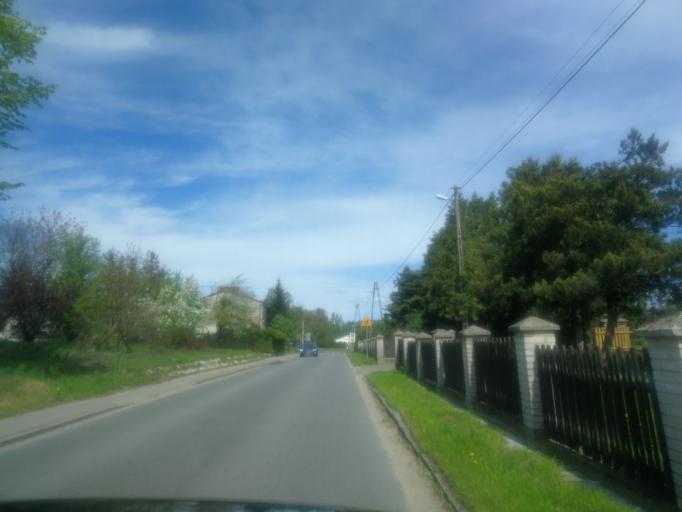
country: PL
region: Warmian-Masurian Voivodeship
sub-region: Powiat ilawski
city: Ilawa
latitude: 53.6619
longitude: 19.6432
